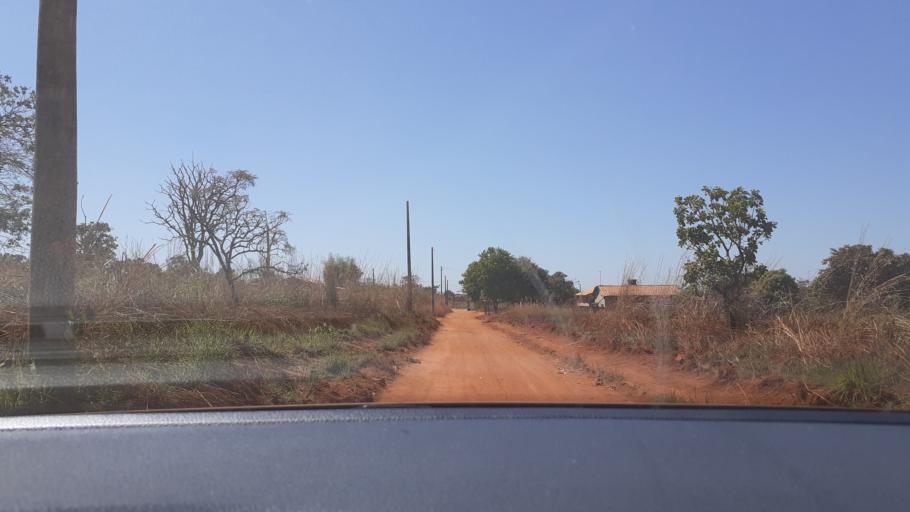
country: BR
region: Goias
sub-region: Aparecida De Goiania
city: Aparecida de Goiania
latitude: -16.8752
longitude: -49.2787
